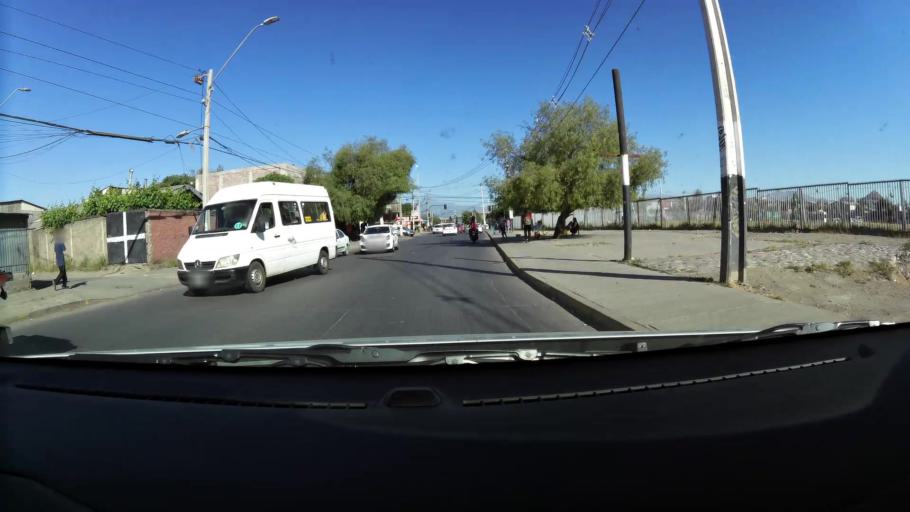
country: CL
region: Santiago Metropolitan
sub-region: Provincia de Maipo
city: San Bernardo
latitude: -33.5930
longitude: -70.6812
